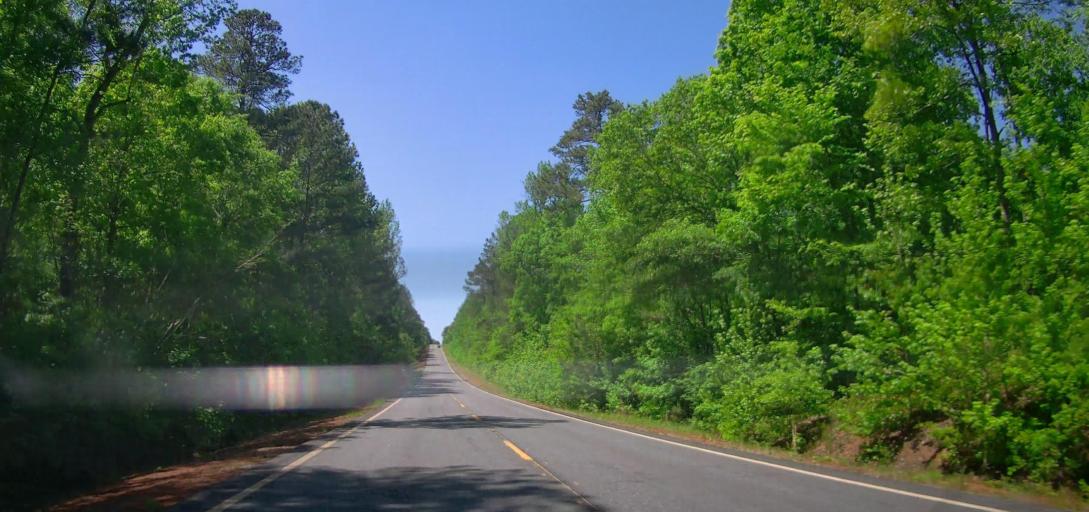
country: US
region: Georgia
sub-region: Putnam County
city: Eatonton
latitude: 33.2106
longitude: -83.4777
